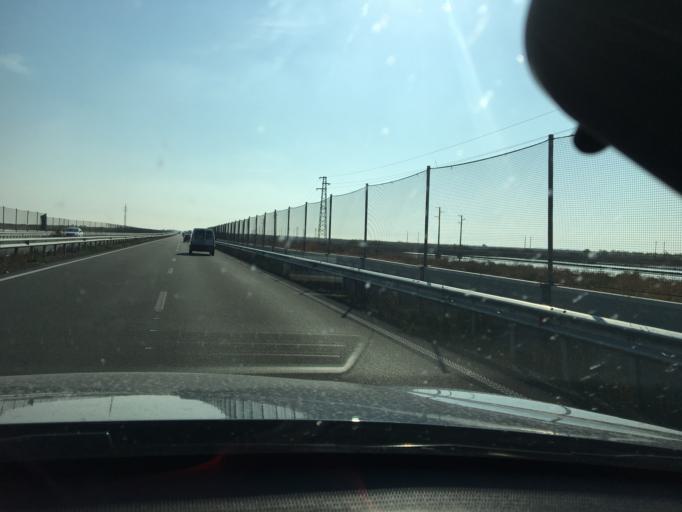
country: BG
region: Burgas
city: Aheloy
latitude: 42.6159
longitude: 27.6242
